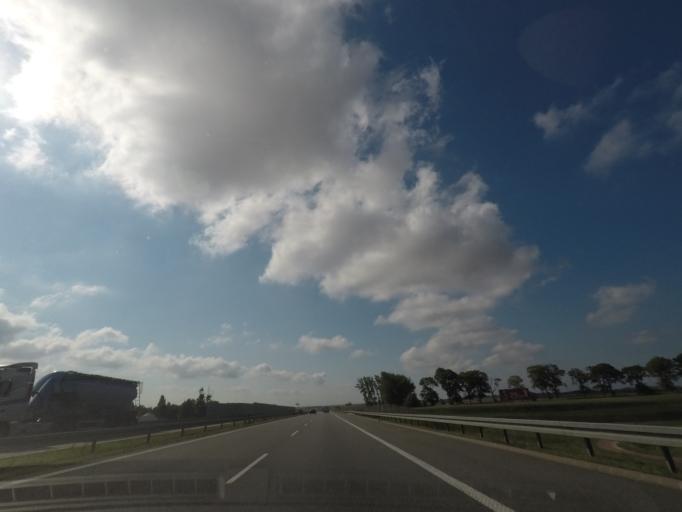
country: PL
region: Pomeranian Voivodeship
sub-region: Powiat gdanski
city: Pszczolki
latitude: 54.1367
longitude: 18.6754
